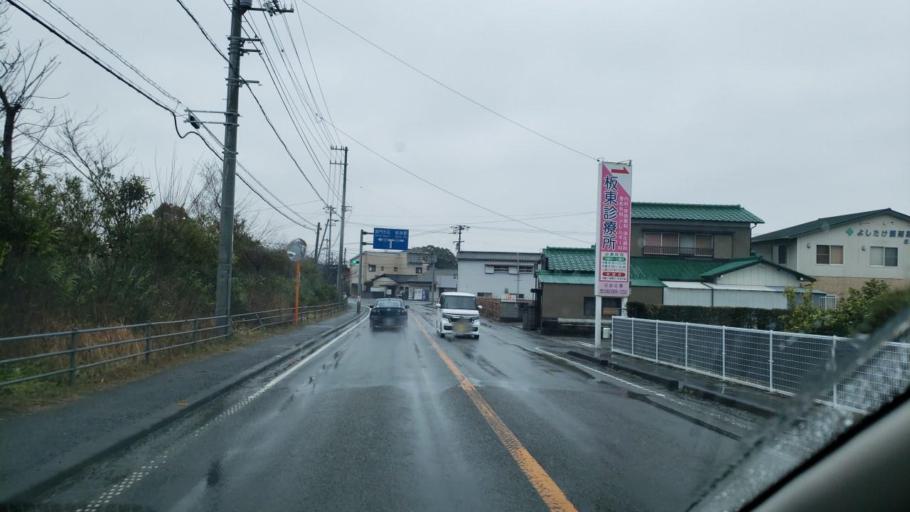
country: JP
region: Tokushima
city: Tokushima-shi
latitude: 34.1575
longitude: 134.5091
